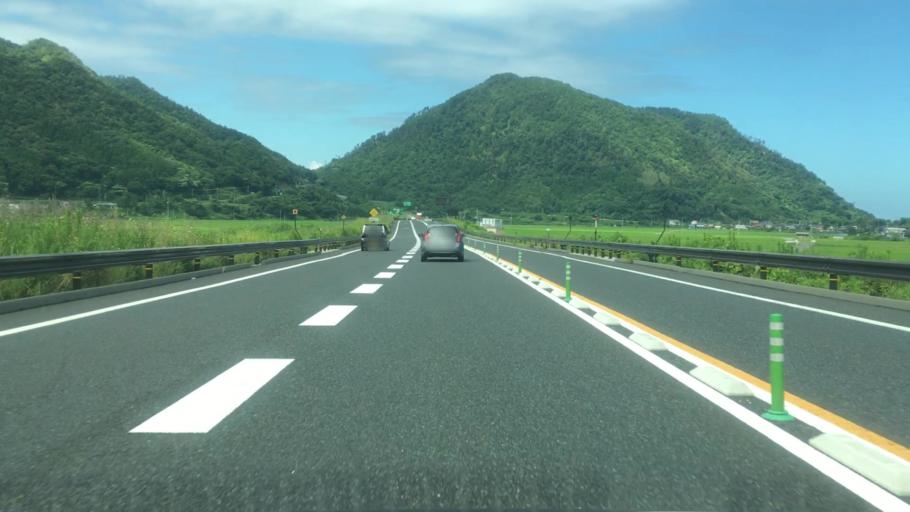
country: JP
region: Tottori
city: Tottori
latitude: 35.5719
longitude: 134.3056
